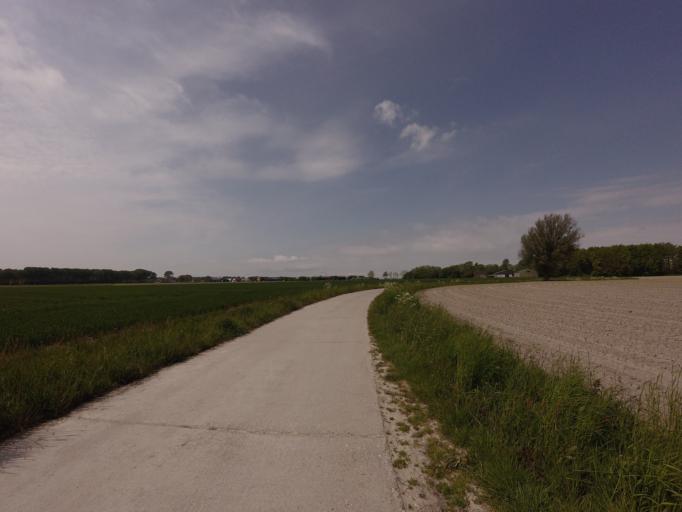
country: NL
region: Friesland
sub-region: Sudwest Fryslan
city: Bolsward
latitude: 53.1075
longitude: 5.4823
